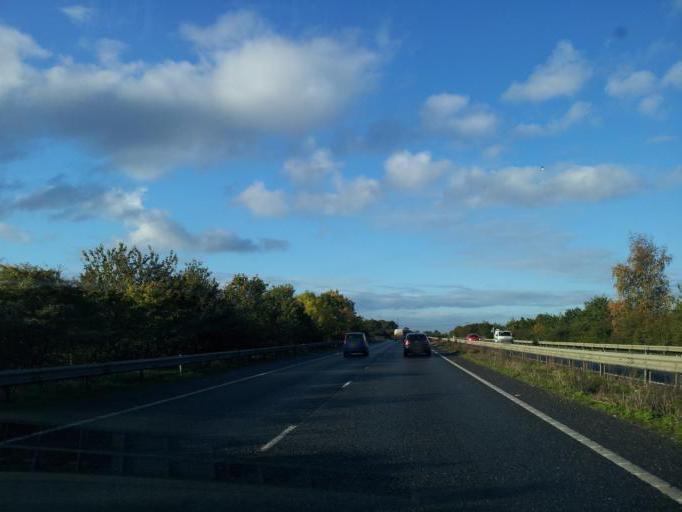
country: GB
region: England
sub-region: Norfolk
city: Cringleford
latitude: 52.5890
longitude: 1.2778
